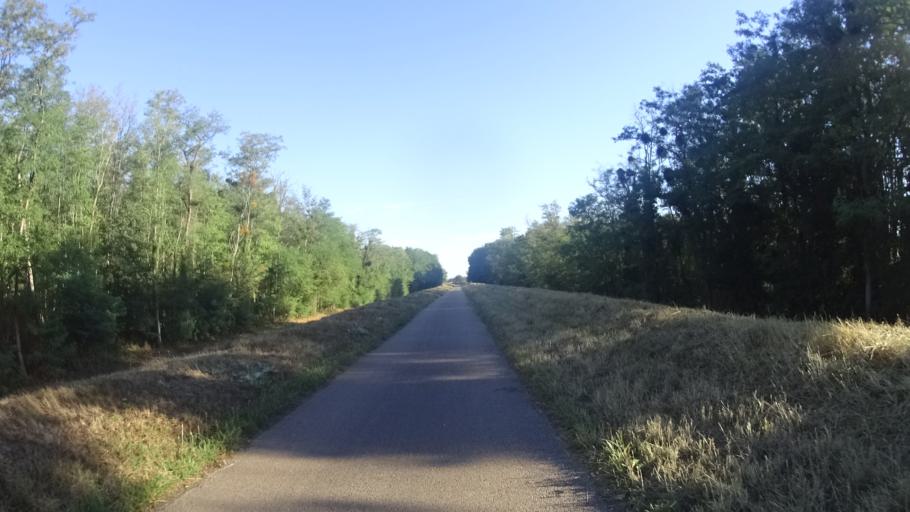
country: FR
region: Centre
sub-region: Departement du Cher
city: Jouet-sur-l'Aubois
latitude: 47.1006
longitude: 3.0250
